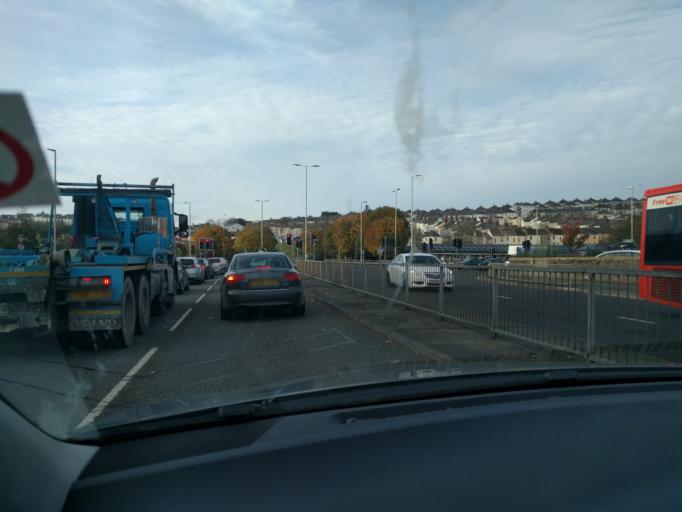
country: GB
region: England
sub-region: Cornwall
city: Torpoint
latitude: 50.3955
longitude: -4.1782
